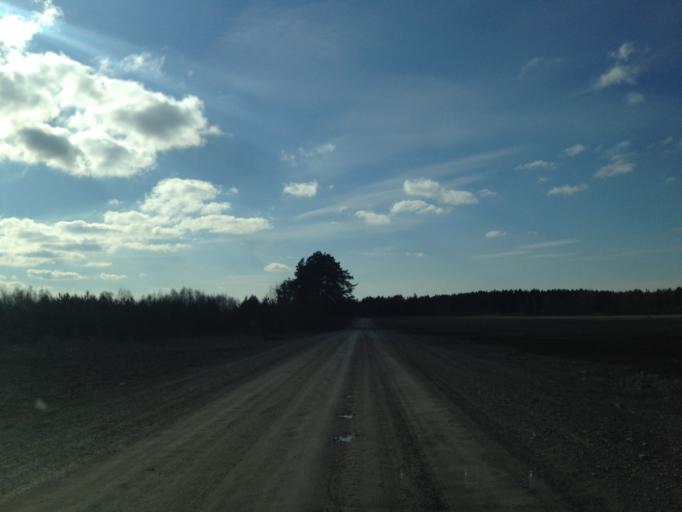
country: EE
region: Harju
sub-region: Nissi vald
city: Riisipere
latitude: 59.1244
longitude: 24.3831
